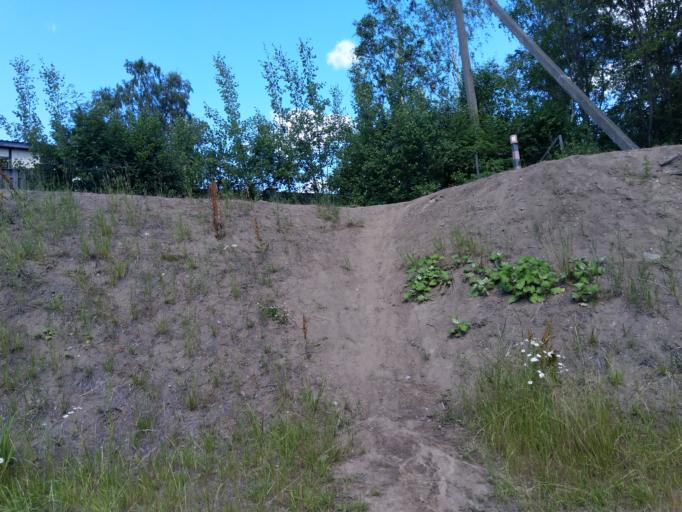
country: RU
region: Leningrad
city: Sapernoye
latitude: 60.6804
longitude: 30.0055
